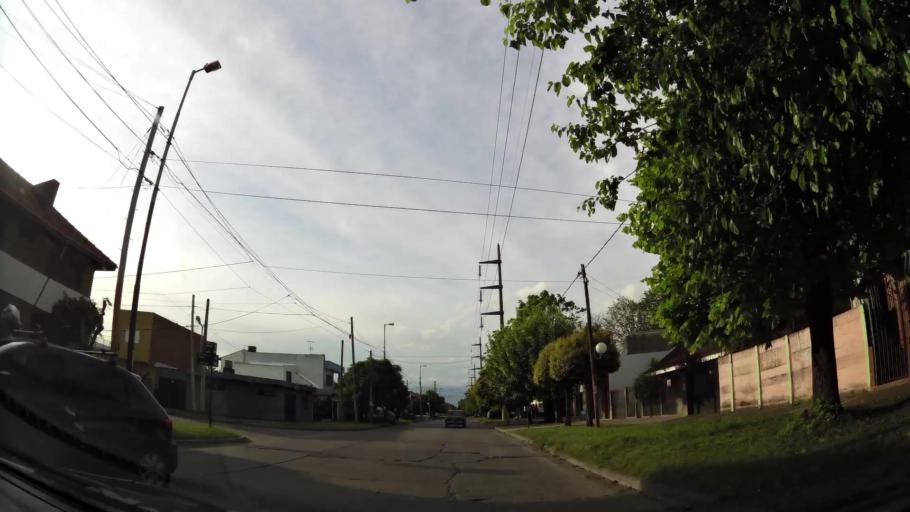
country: AR
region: Buenos Aires
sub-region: Partido de Quilmes
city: Quilmes
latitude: -34.7398
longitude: -58.2697
